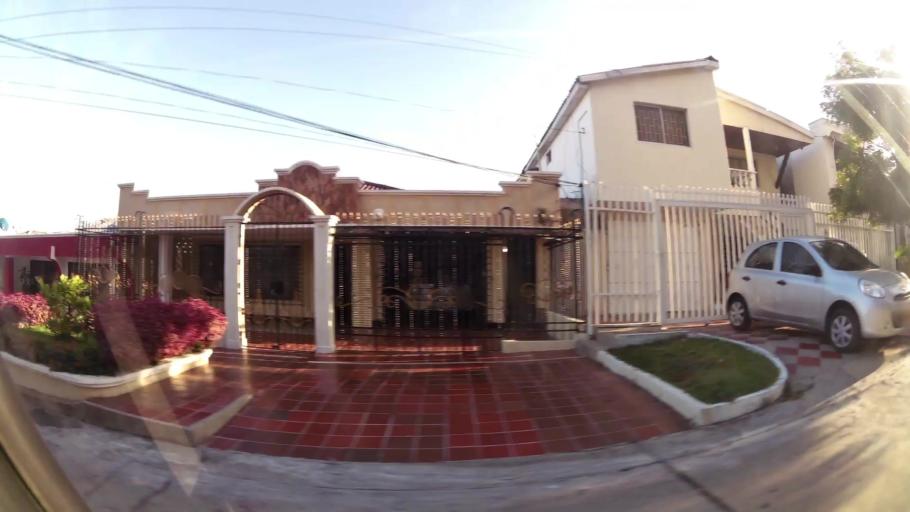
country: CO
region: Atlantico
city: Barranquilla
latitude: 10.9853
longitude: -74.8030
